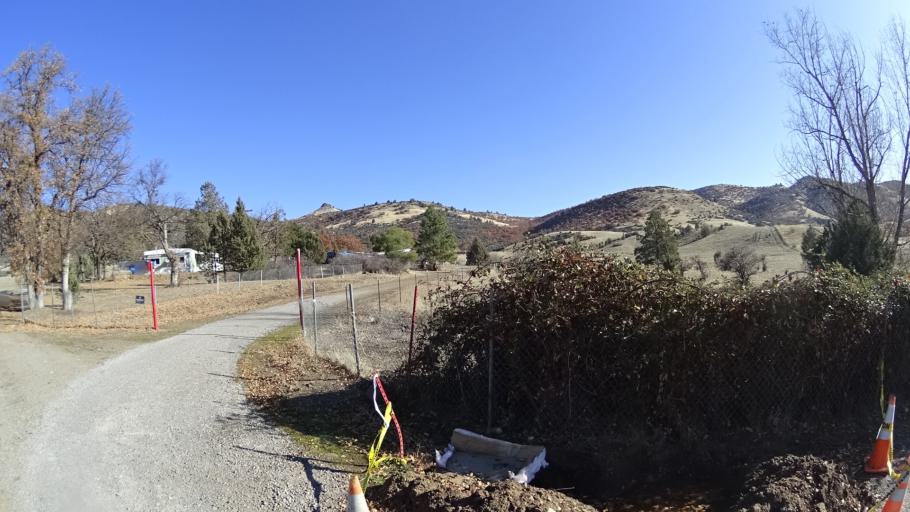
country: US
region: California
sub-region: Siskiyou County
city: Montague
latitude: 41.9159
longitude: -122.5586
